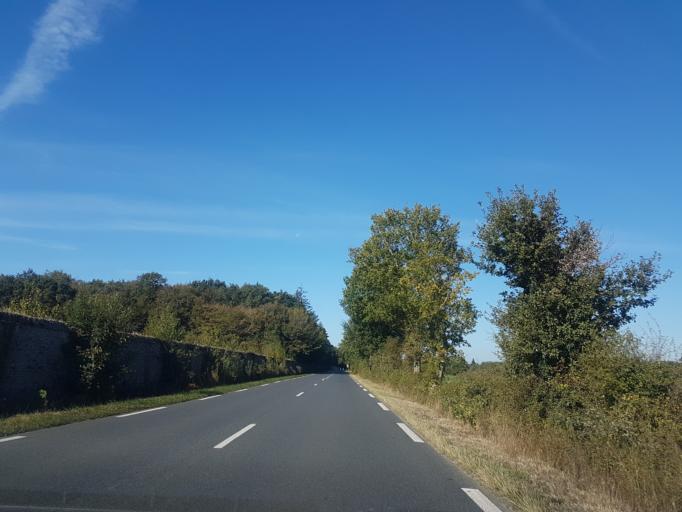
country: FR
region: Pays de la Loire
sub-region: Departement de la Loire-Atlantique
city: Nort-sur-Erdre
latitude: 47.4170
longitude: -1.4769
